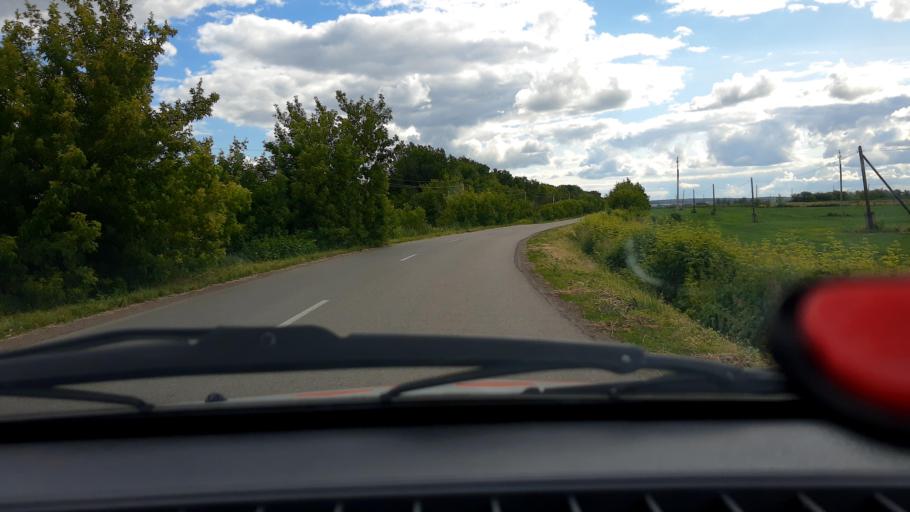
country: RU
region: Bashkortostan
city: Kabakovo
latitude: 54.5126
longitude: 55.9417
